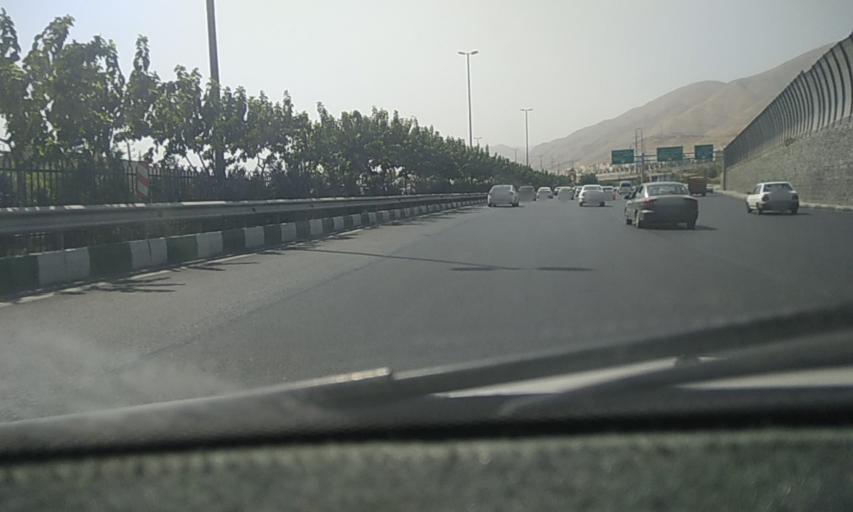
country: IR
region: Tehran
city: Shahr-e Qods
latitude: 35.7578
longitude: 51.2617
